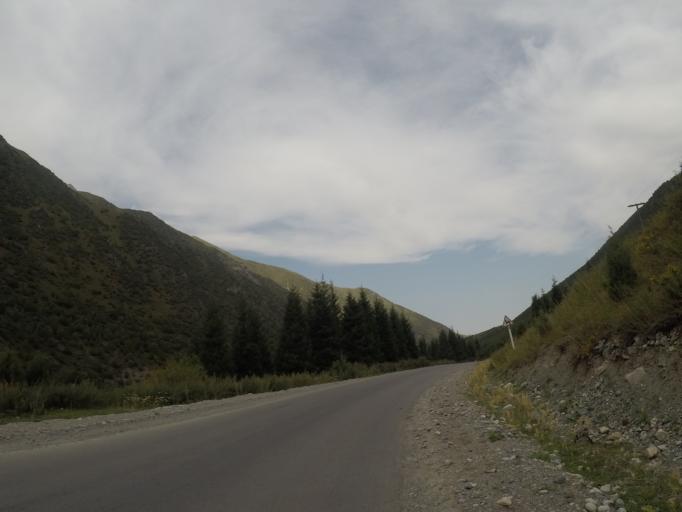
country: KG
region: Chuy
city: Bishkek
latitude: 42.5908
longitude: 74.4832
